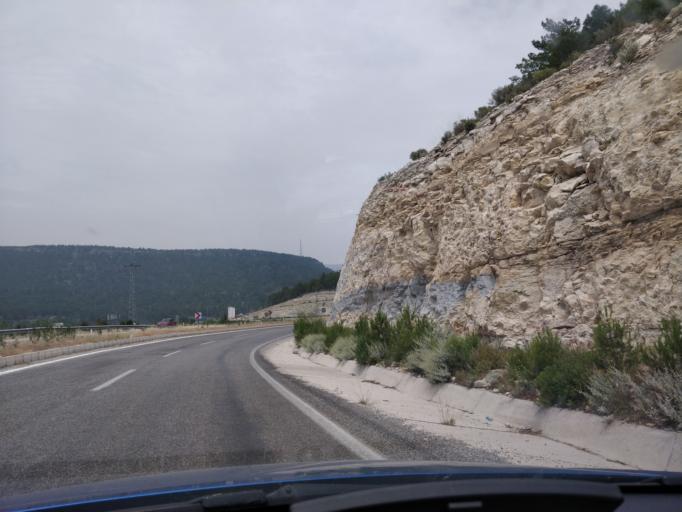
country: TR
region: Mersin
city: Tasucu
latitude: 36.3948
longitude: 33.8432
